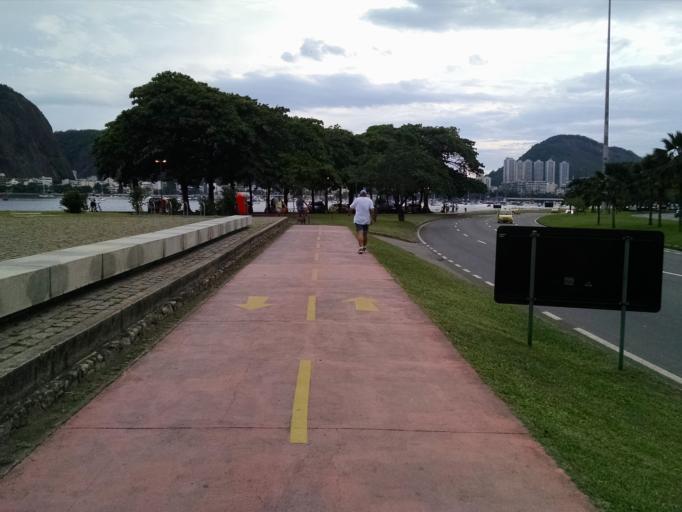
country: BR
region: Rio de Janeiro
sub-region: Rio De Janeiro
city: Rio de Janeiro
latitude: -22.9397
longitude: -43.1701
